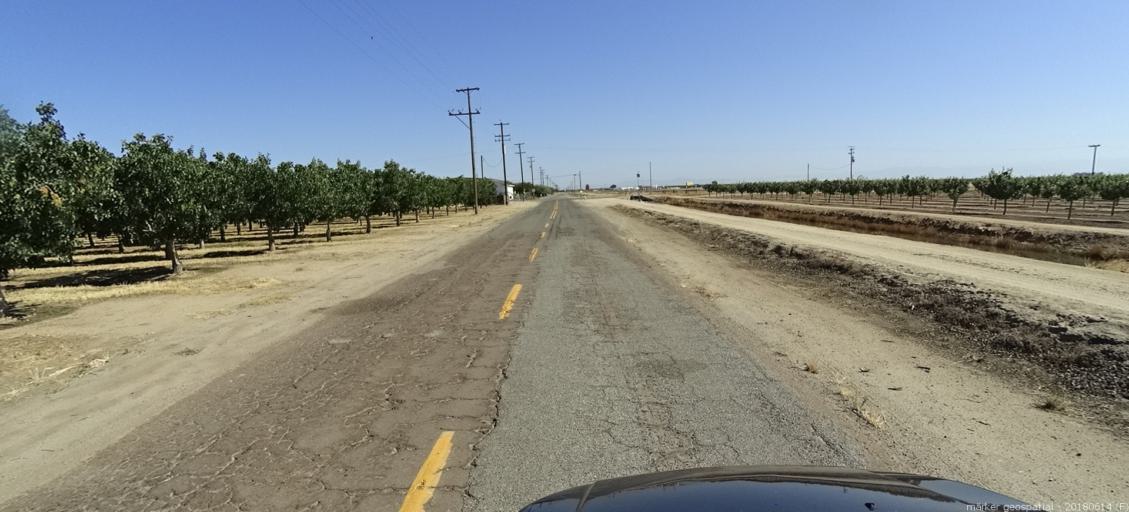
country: US
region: California
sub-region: Madera County
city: Fairmead
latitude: 37.0388
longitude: -120.1660
